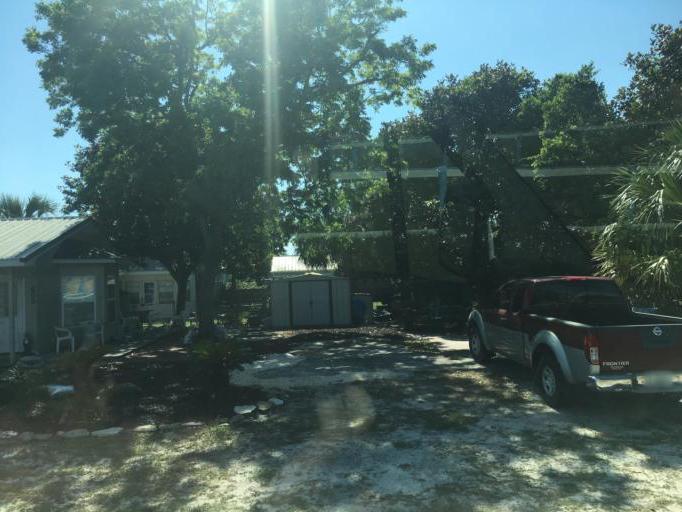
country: US
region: Florida
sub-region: Bay County
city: Panama City Beach
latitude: 30.2008
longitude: -85.8440
